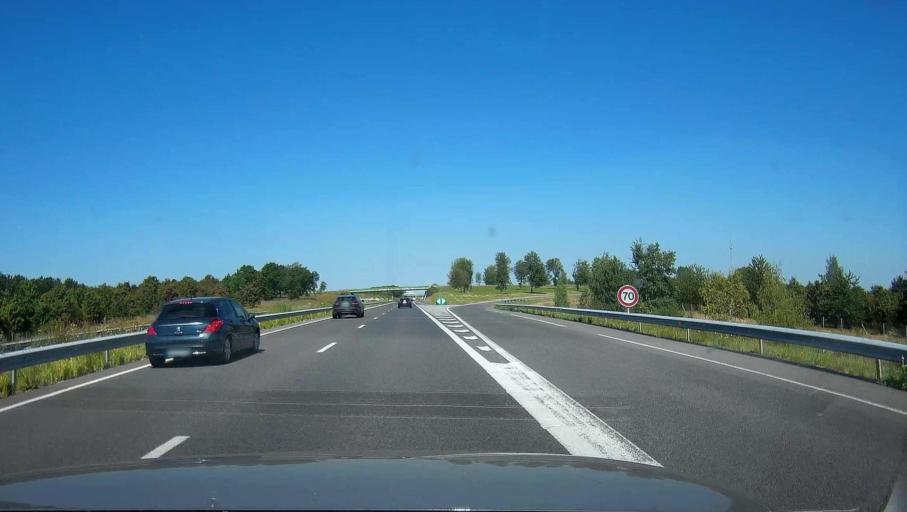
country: FR
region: Champagne-Ardenne
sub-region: Departement de la Marne
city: Fagnieres
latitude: 48.9043
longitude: 4.2849
